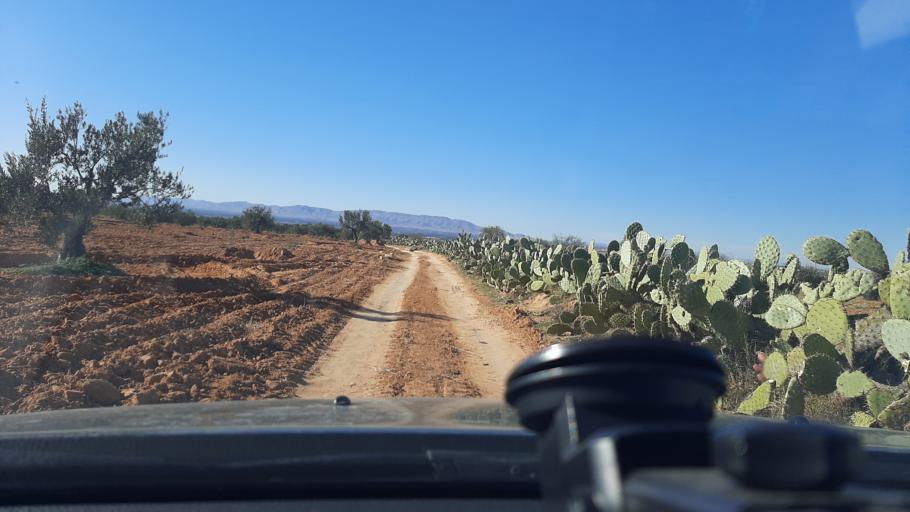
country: TN
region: Safaqis
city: Bi'r `Ali Bin Khalifah
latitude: 34.9990
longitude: 10.0904
